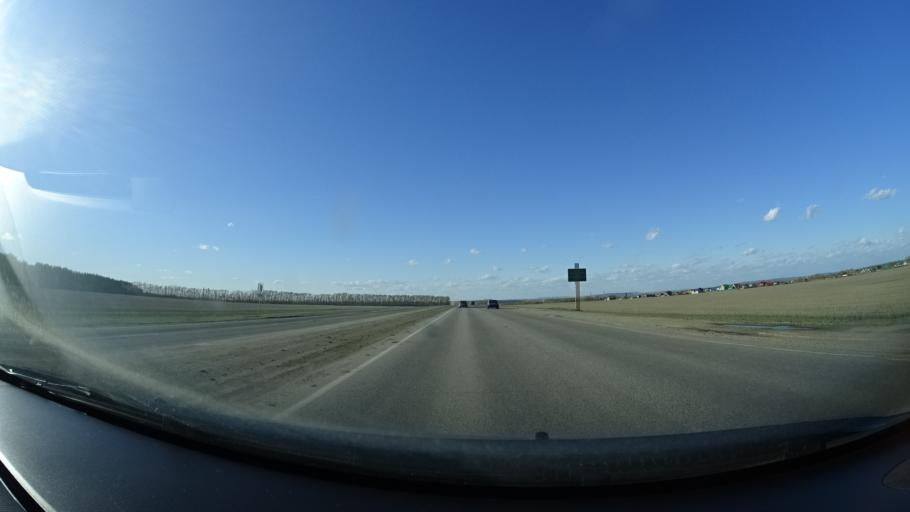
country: RU
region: Bashkortostan
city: Kabakovo
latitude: 54.4645
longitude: 55.9145
